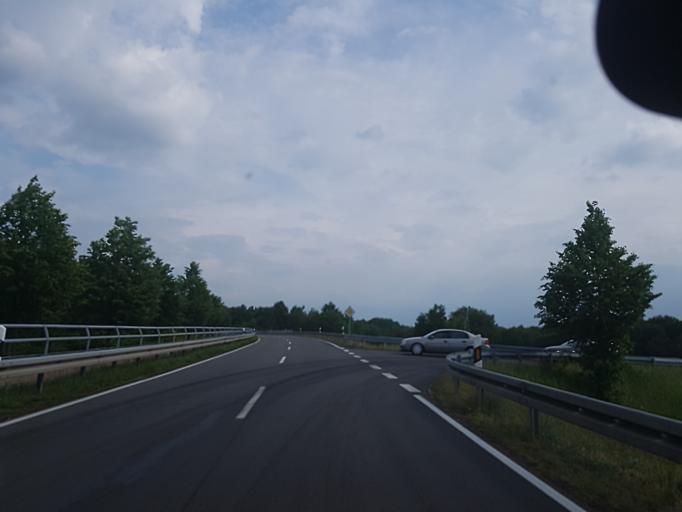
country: DE
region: Saxony-Anhalt
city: Coswig
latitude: 51.9071
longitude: 12.4170
